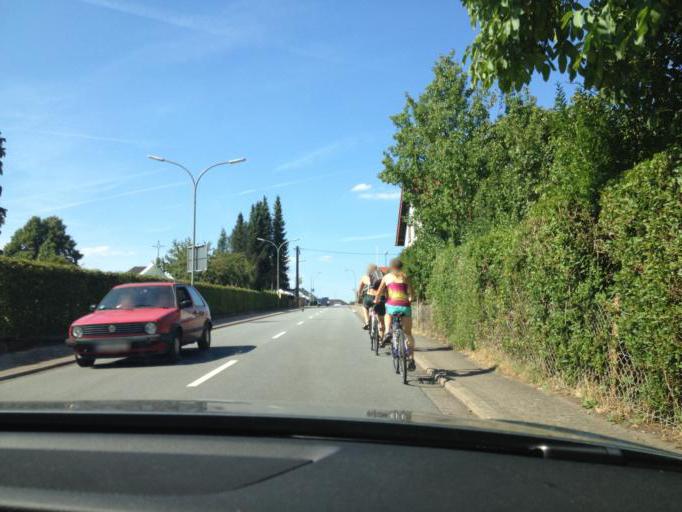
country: DE
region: Saarland
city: Oberthal
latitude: 49.5496
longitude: 7.0610
